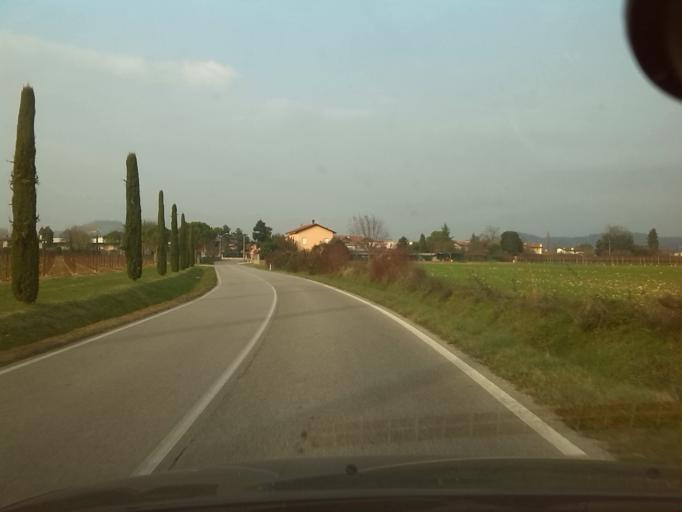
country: IT
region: Friuli Venezia Giulia
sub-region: Provincia di Udine
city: Corno di Rosazzo
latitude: 45.9824
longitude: 13.4315
